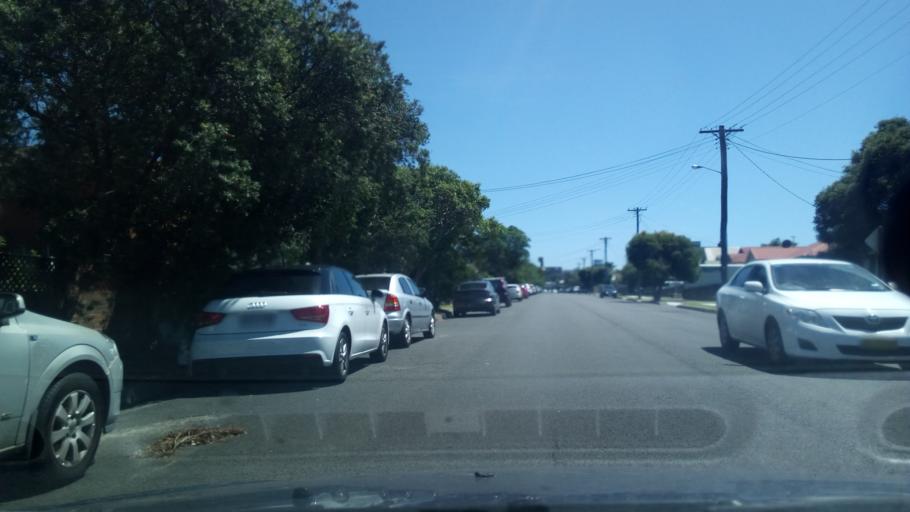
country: AU
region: New South Wales
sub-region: Wollongong
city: Wollongong
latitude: -34.4322
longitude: 150.8912
